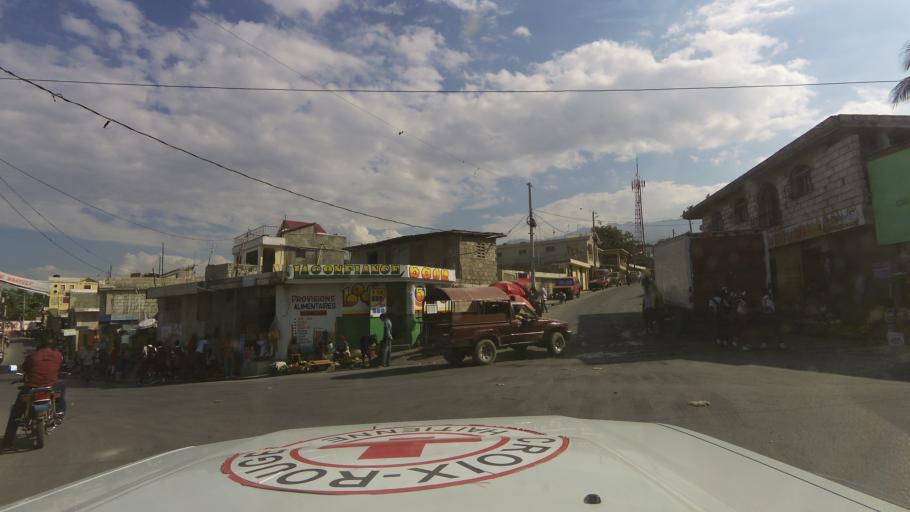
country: HT
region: Ouest
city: Petionville
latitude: 18.5273
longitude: -72.2819
